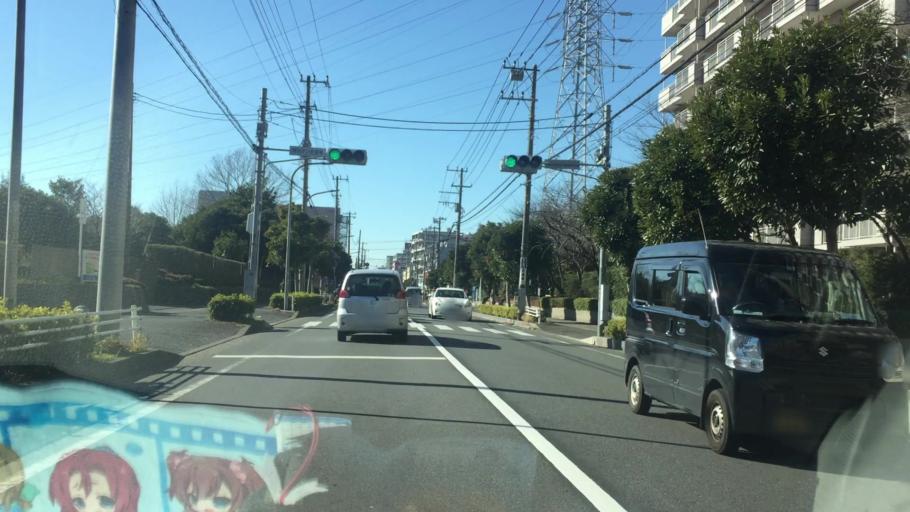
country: JP
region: Tokyo
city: Urayasu
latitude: 35.6704
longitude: 139.9091
